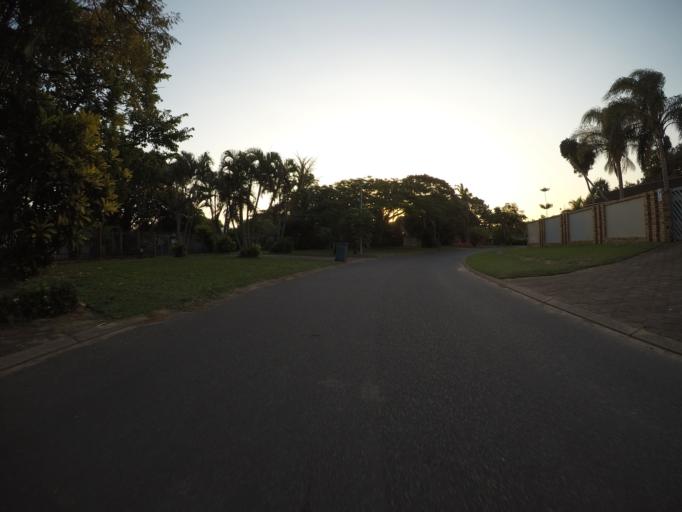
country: ZA
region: KwaZulu-Natal
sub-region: uThungulu District Municipality
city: Richards Bay
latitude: -28.7693
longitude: 32.1146
